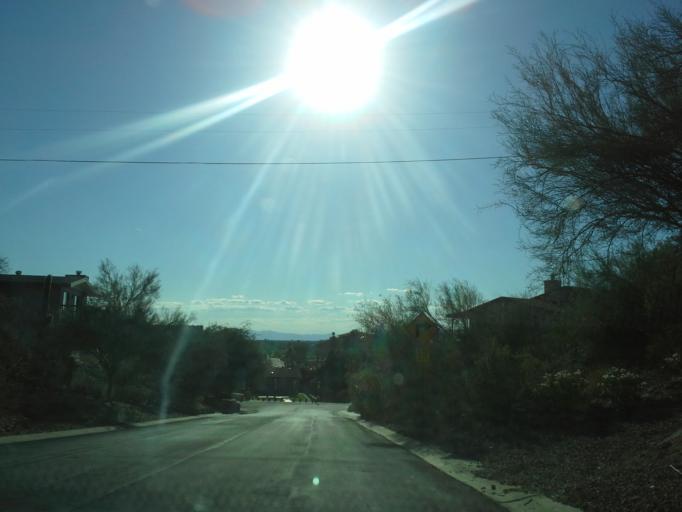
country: US
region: Arizona
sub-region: Maricopa County
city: Paradise Valley
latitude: 33.5600
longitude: -112.0518
